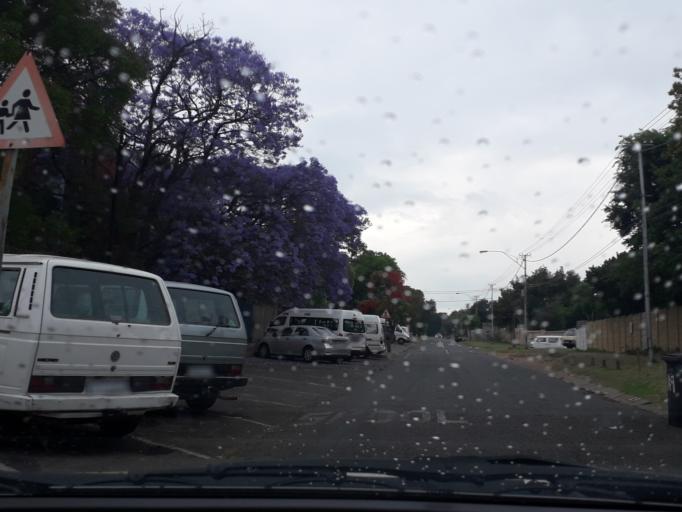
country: ZA
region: Gauteng
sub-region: City of Johannesburg Metropolitan Municipality
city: Modderfontein
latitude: -26.1335
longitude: 28.1032
